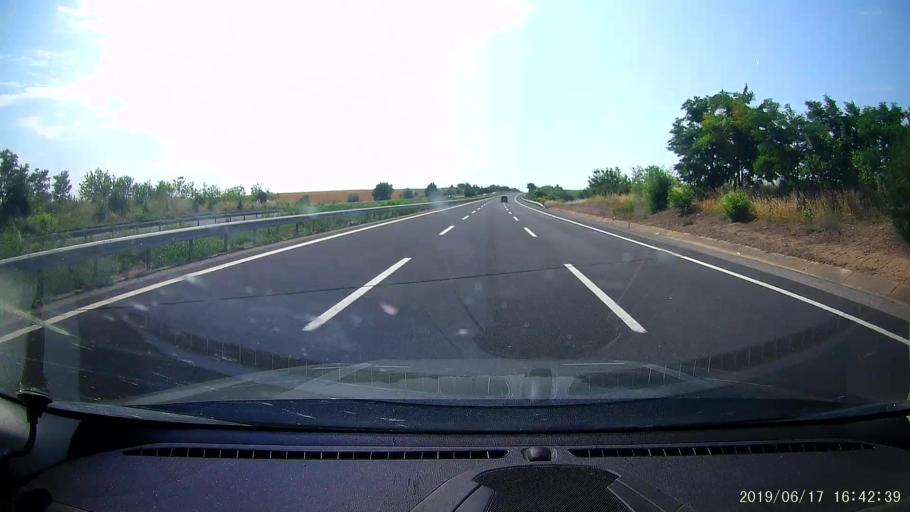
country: TR
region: Kirklareli
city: Luleburgaz
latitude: 41.4743
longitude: 27.3172
